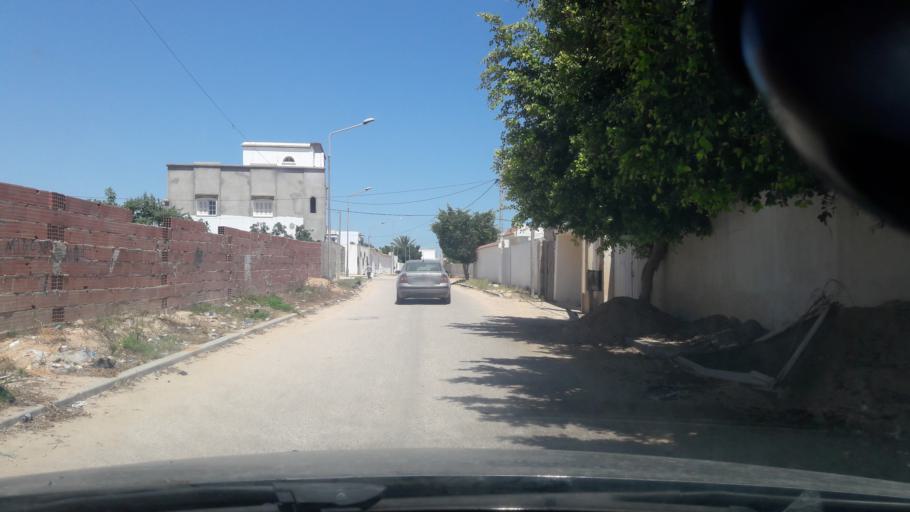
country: TN
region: Safaqis
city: Al Qarmadah
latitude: 34.8090
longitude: 10.7523
